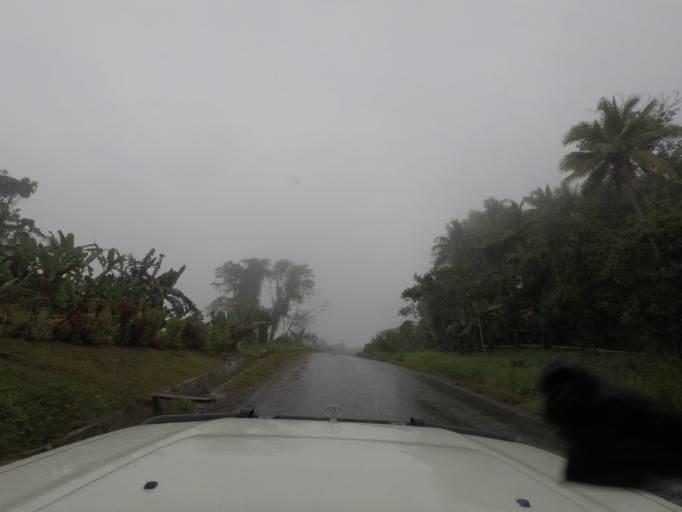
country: PG
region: Madang
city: Madang
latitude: -5.4503
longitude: 145.5093
